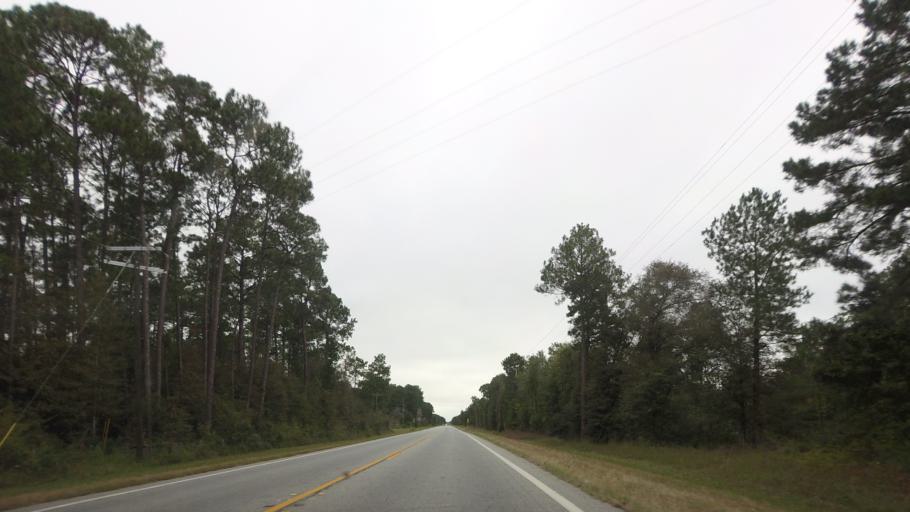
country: US
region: Georgia
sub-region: Berrien County
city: Nashville
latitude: 31.1448
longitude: -83.2182
